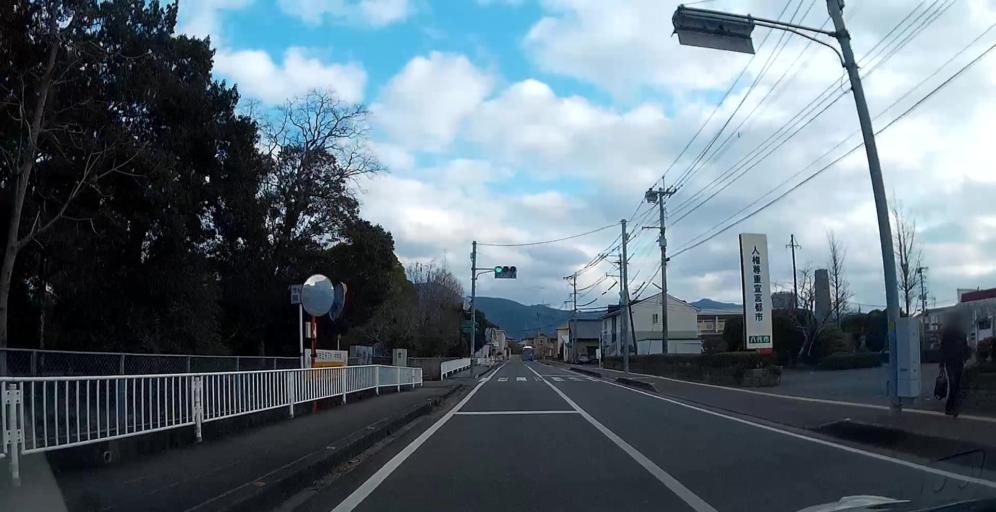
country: JP
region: Kumamoto
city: Yatsushiro
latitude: 32.5356
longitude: 130.6342
